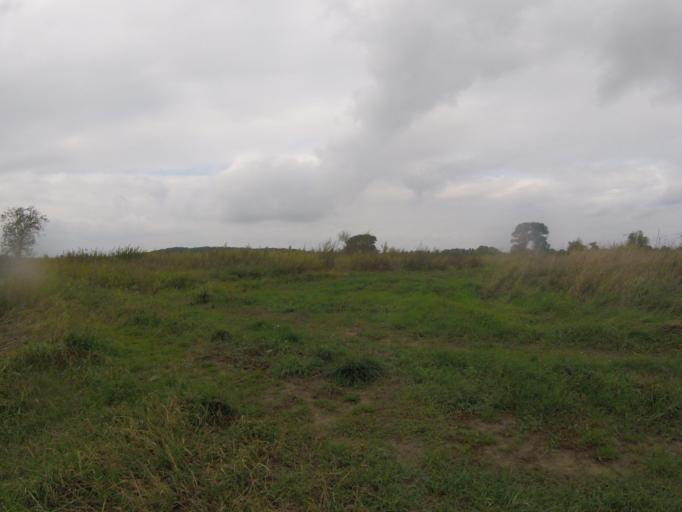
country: DE
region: Brandenburg
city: Mittenwalde
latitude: 52.2559
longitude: 13.5151
